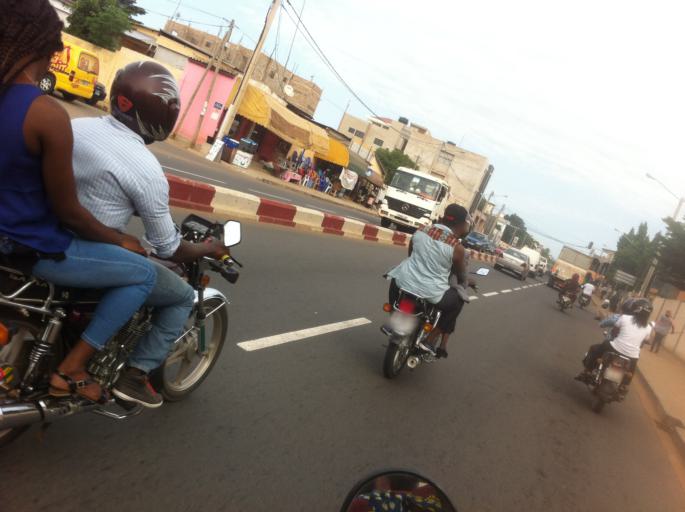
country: TG
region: Maritime
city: Lome
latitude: 6.1465
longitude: 1.2038
